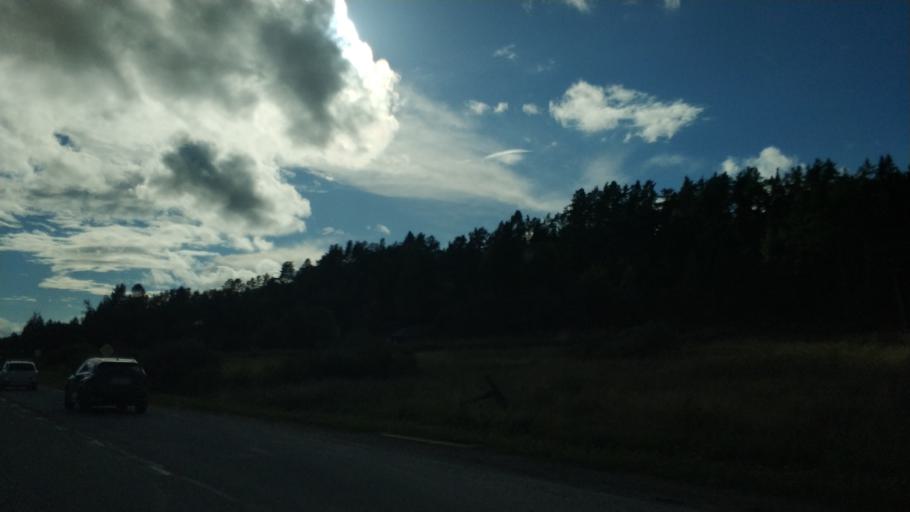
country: RU
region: Republic of Karelia
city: Lakhdenpokh'ya
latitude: 61.5564
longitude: 30.3249
